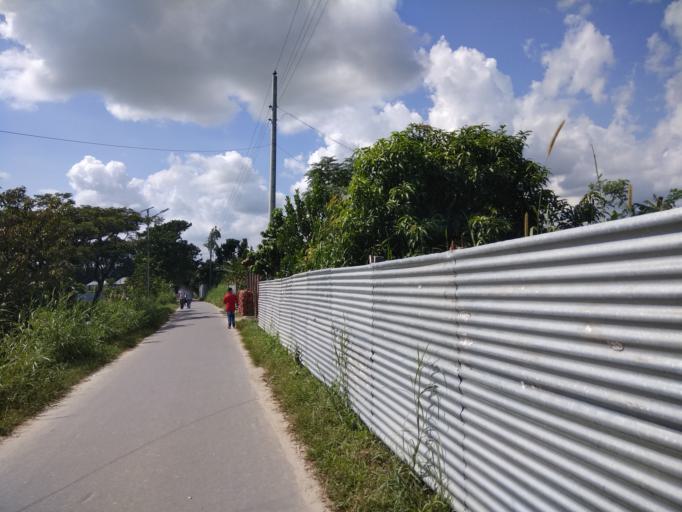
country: BD
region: Dhaka
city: Narayanganj
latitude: 23.4440
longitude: 90.4559
